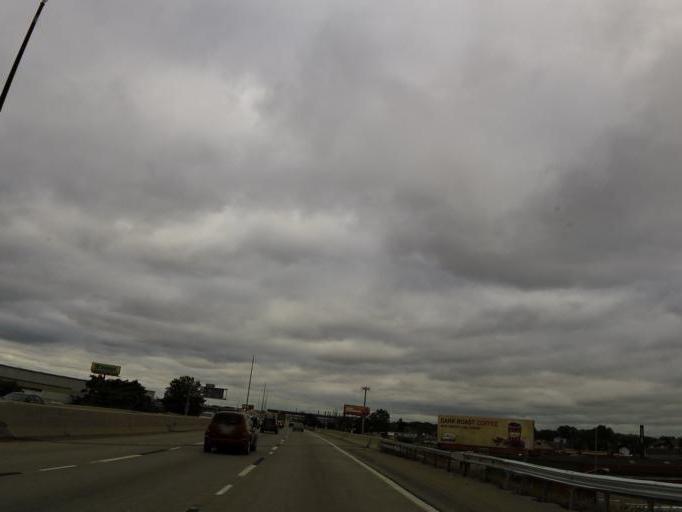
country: US
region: New York
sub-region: Erie County
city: West Seneca
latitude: 42.8678
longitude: -78.8284
